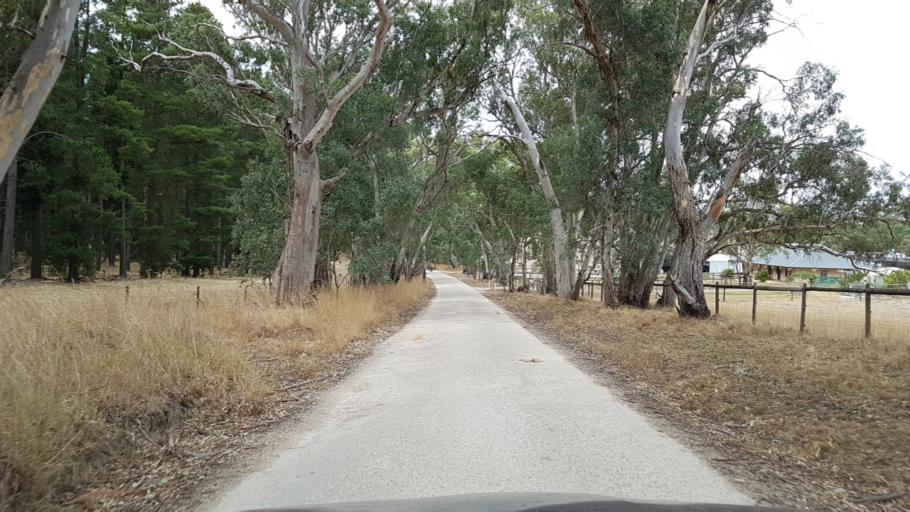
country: AU
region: South Australia
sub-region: Adelaide Hills
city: Birdwood
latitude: -34.7850
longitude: 138.9801
